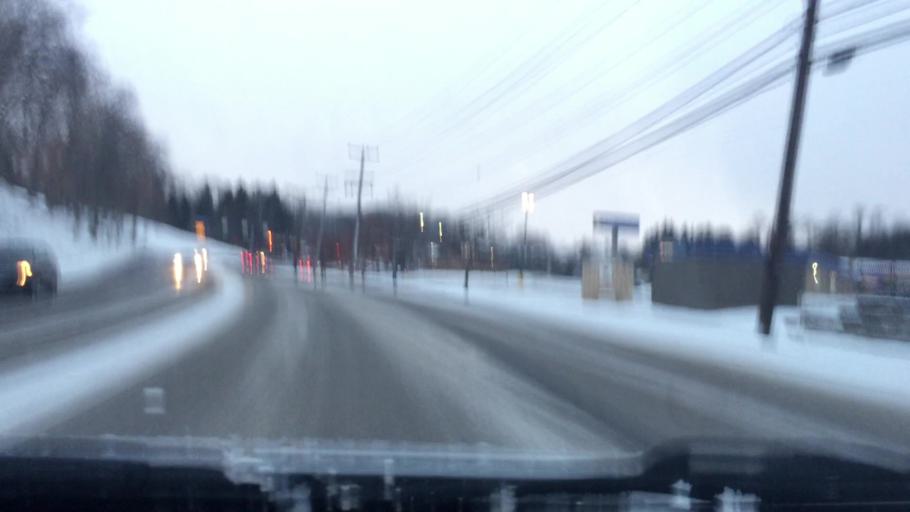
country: US
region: Pennsylvania
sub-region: Allegheny County
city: Carnot-Moon
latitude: 40.5218
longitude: -80.2176
